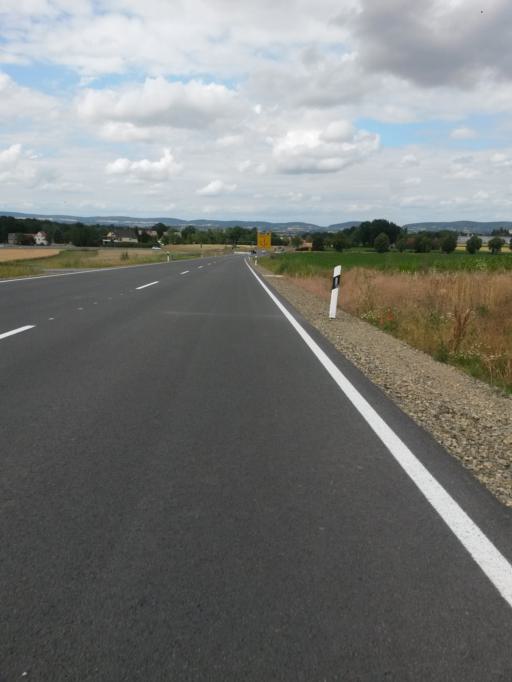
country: DE
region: North Rhine-Westphalia
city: Loehne
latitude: 52.1704
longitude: 8.7494
